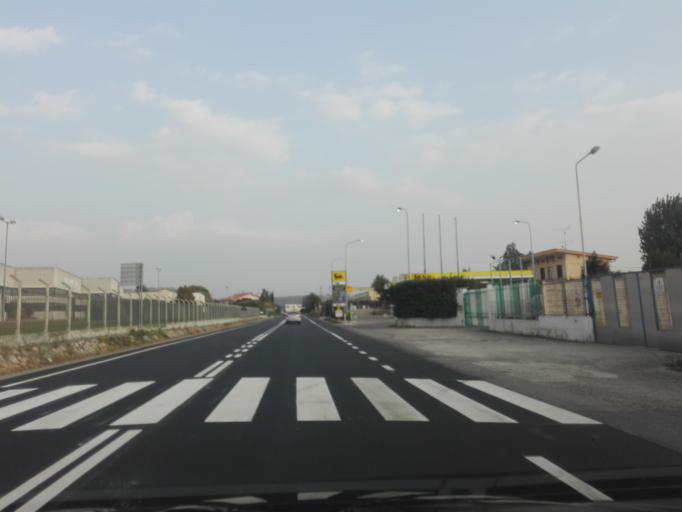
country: IT
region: Veneto
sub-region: Provincia di Verona
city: Pastrengo
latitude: 45.4883
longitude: 10.7717
